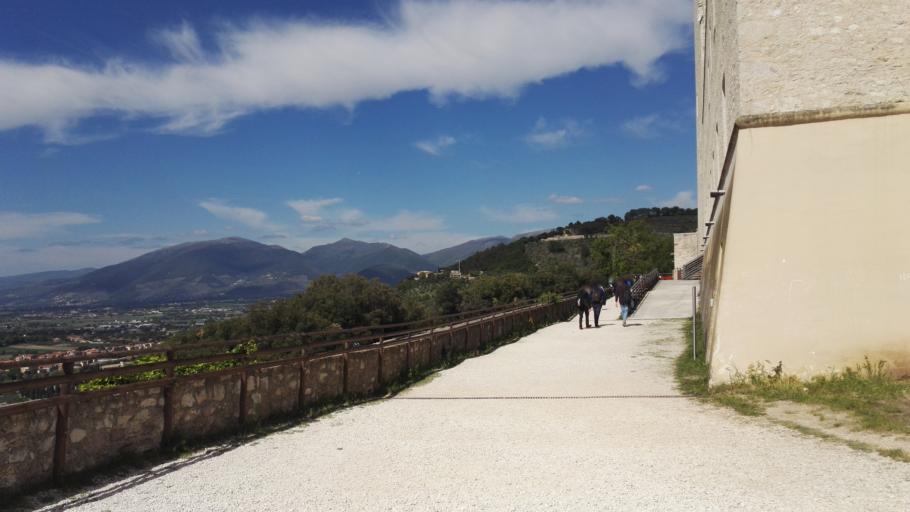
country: IT
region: Umbria
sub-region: Provincia di Perugia
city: Spoleto
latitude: 42.7340
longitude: 12.7411
